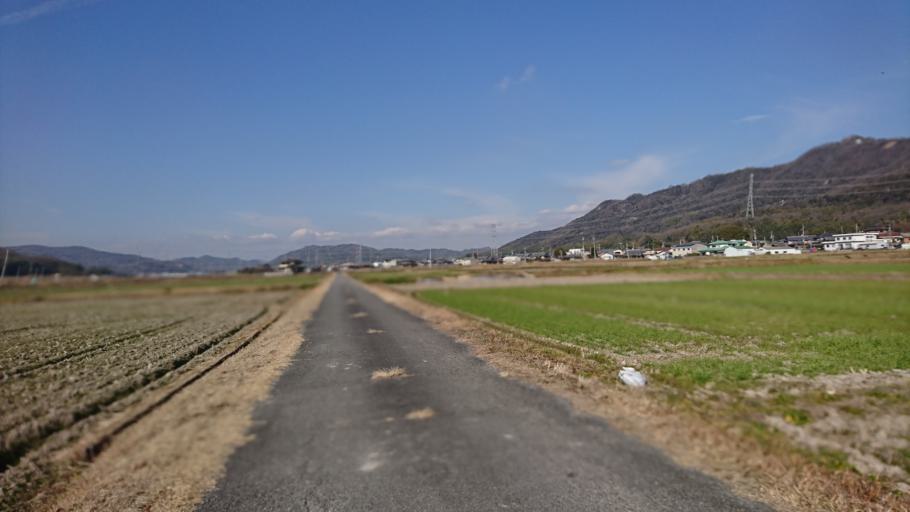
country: JP
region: Hyogo
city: Kakogawacho-honmachi
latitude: 34.8173
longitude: 134.8521
